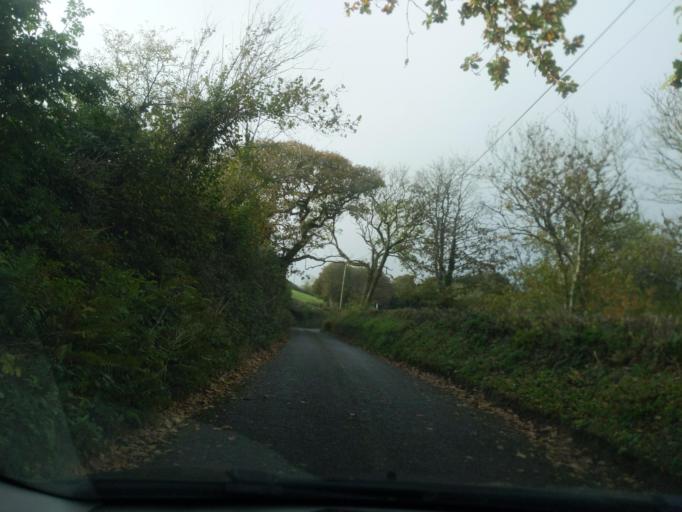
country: GB
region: England
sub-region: Cornwall
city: Looe
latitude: 50.3668
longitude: -4.4006
